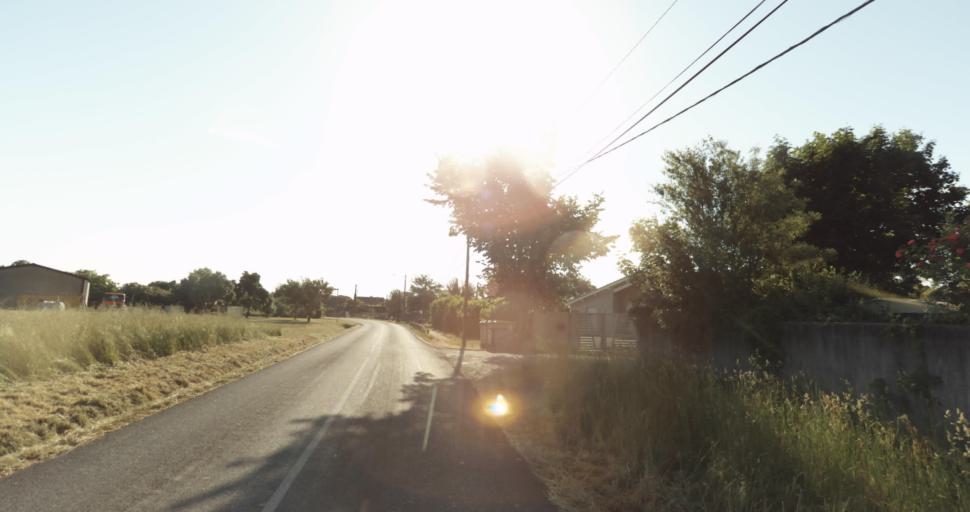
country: FR
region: Midi-Pyrenees
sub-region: Departement de la Haute-Garonne
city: Fonsorbes
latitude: 43.5676
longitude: 1.2281
